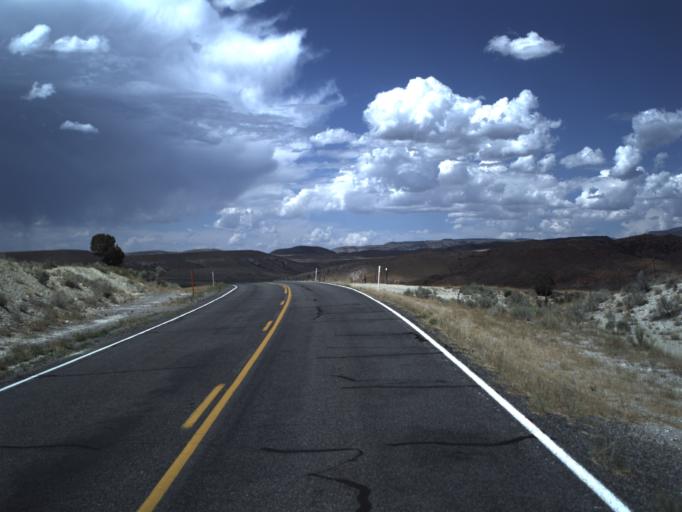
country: US
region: Utah
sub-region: Sanpete County
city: Gunnison
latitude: 39.1449
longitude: -111.7355
